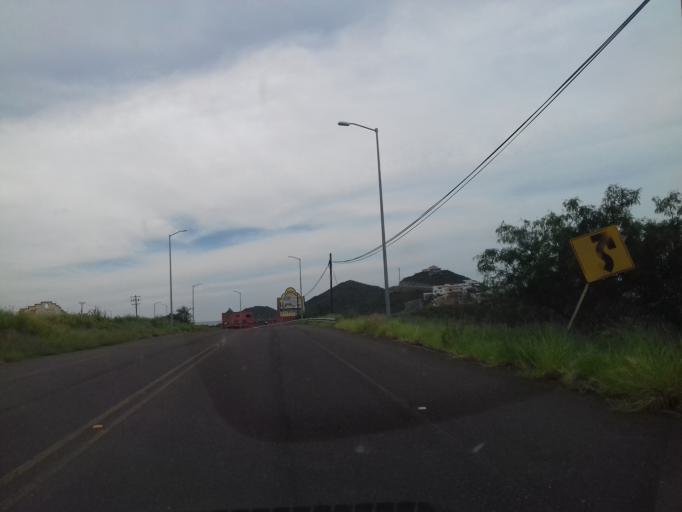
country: MX
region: Sonora
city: Heroica Guaymas
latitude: 27.9471
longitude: -111.0860
